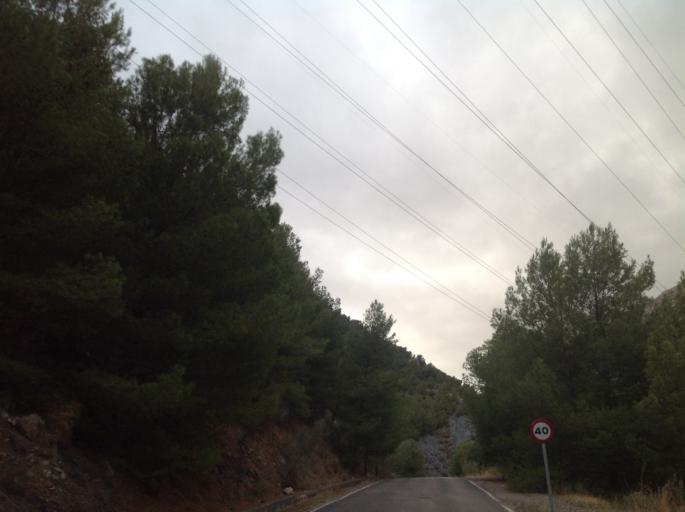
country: ES
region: Andalusia
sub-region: Provincia de Malaga
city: Carratraca
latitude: 36.9058
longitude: -4.7625
